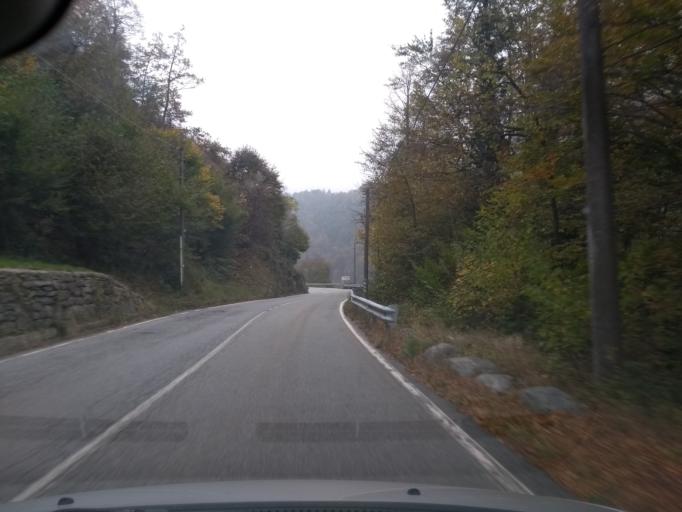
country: IT
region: Piedmont
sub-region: Provincia di Torino
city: Ceres
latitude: 45.3086
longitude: 7.3951
